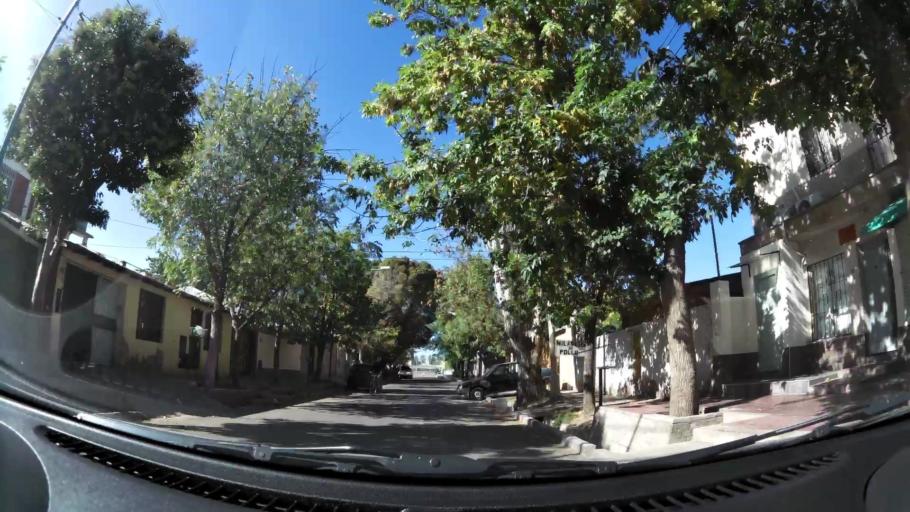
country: AR
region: Mendoza
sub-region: Departamento de Godoy Cruz
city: Godoy Cruz
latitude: -32.9337
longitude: -68.8609
